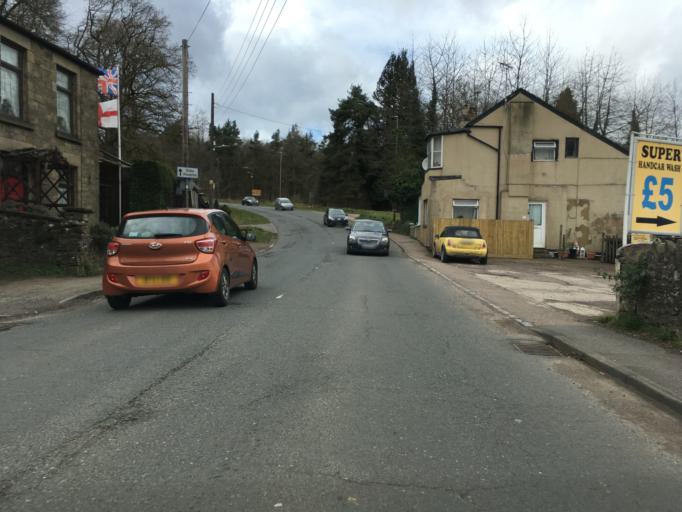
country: GB
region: England
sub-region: Gloucestershire
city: Cinderford
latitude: 51.8111
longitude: -2.5085
